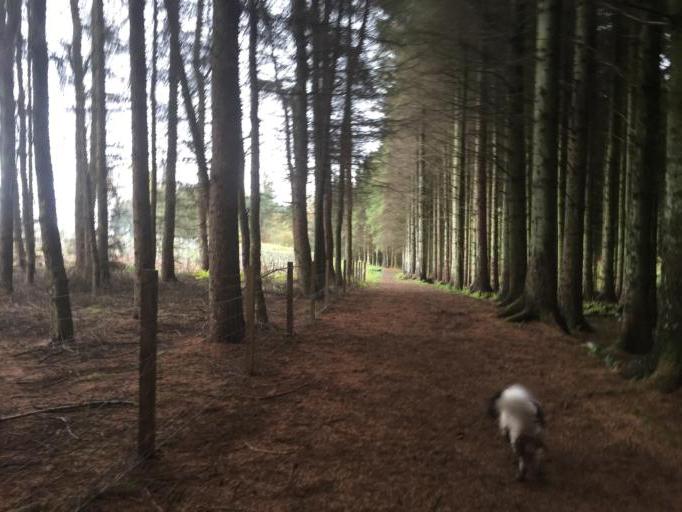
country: GB
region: Scotland
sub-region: West Lothian
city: Linlithgow
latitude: 55.9533
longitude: -3.6010
